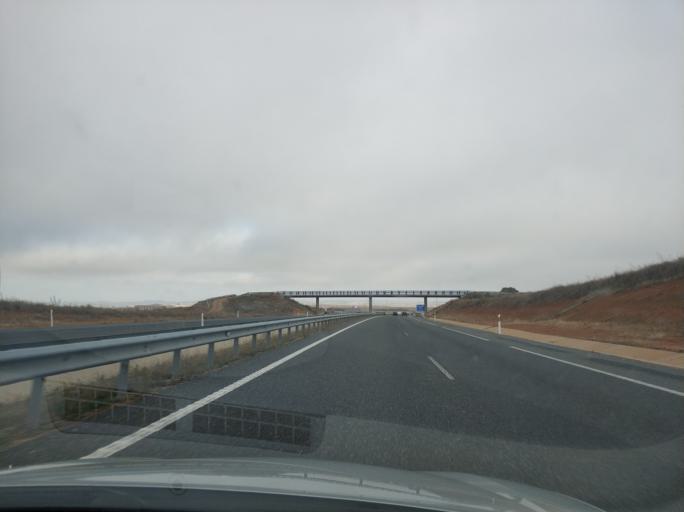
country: ES
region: Castille and Leon
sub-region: Provincia de Leon
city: Valdefresno
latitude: 42.5630
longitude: -5.5104
